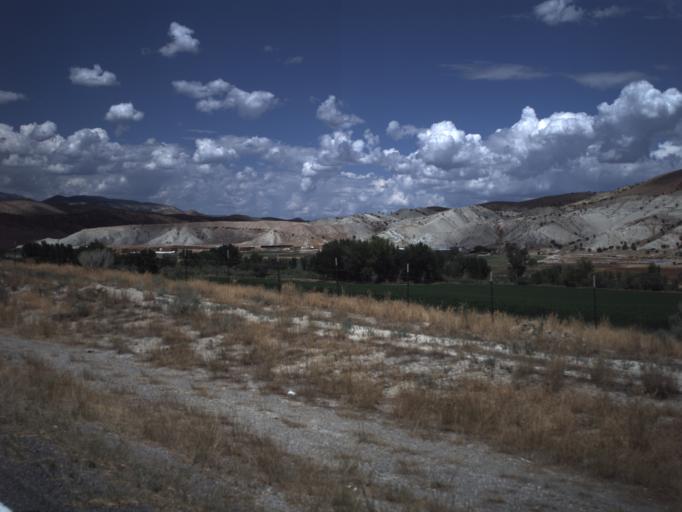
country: US
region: Utah
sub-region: Sanpete County
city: Gunnison
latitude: 39.1401
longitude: -111.7320
